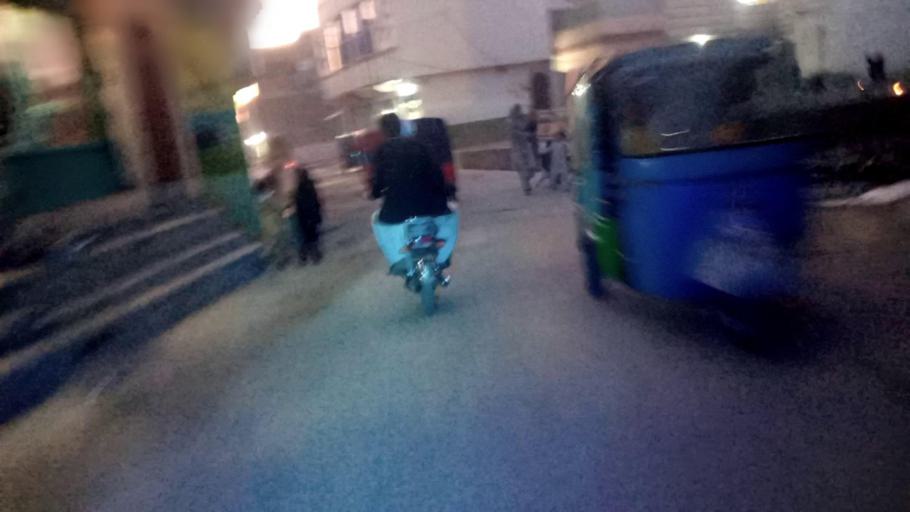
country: PK
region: Khyber Pakhtunkhwa
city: Mingora
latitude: 34.7768
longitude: 72.3394
